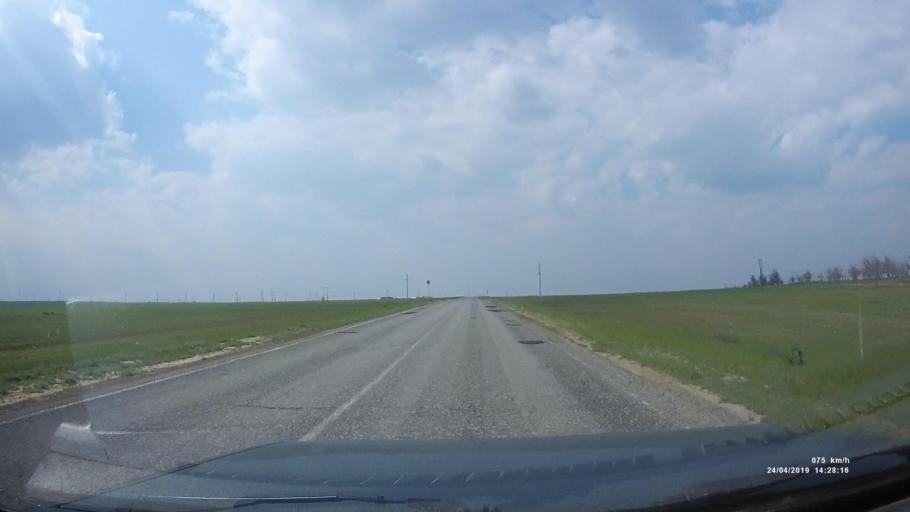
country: RU
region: Kalmykiya
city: Arshan'
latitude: 46.3379
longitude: 44.0321
